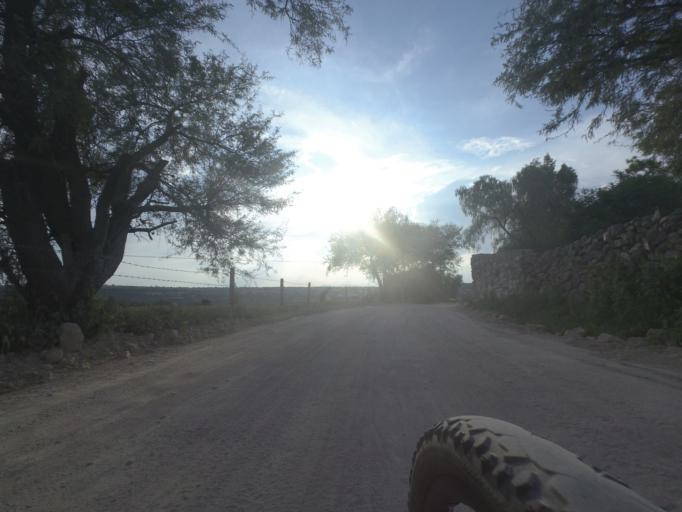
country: MX
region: Aguascalientes
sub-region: Aguascalientes
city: La Loma de los Negritos
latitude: 21.7755
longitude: -102.3701
